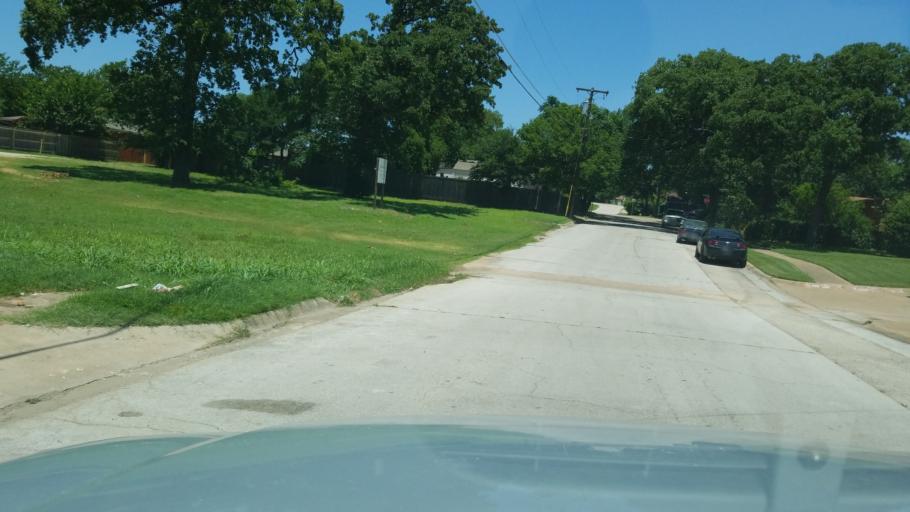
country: US
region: Texas
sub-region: Dallas County
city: Irving
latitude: 32.8004
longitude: -96.9142
